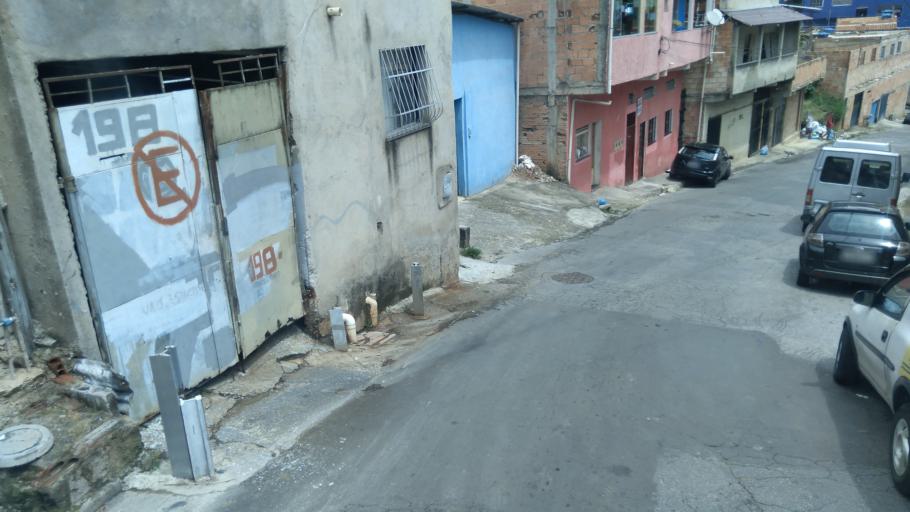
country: BR
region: Minas Gerais
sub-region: Belo Horizonte
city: Belo Horizonte
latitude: -19.8498
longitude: -43.8915
